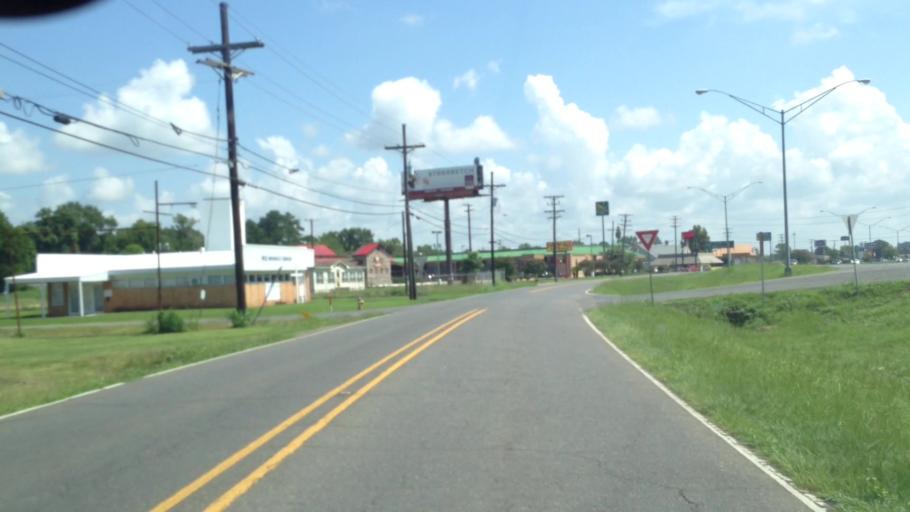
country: US
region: Louisiana
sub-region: Rapides Parish
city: Alexandria
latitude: 31.3084
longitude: -92.4797
